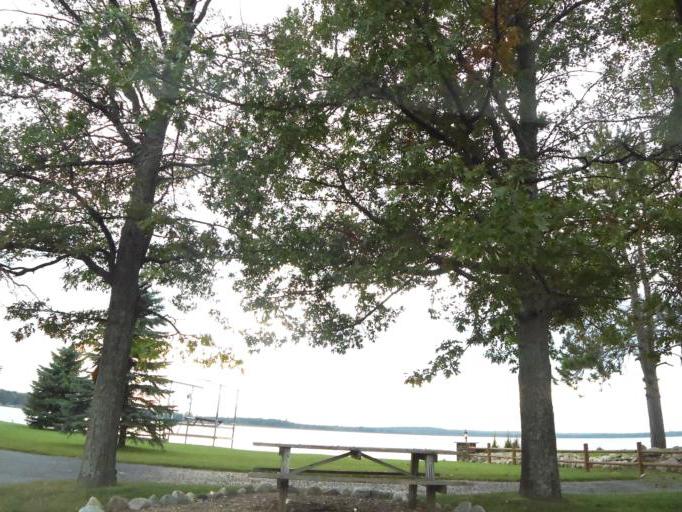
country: US
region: Michigan
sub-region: Roscommon County
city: Saint Helen
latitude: 44.3590
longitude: -84.4735
